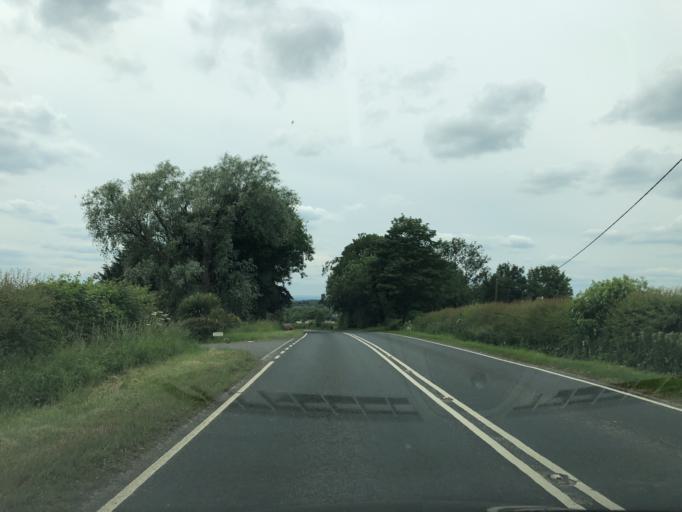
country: GB
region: England
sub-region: North Yorkshire
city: Thirsk
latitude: 54.2345
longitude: -1.3158
